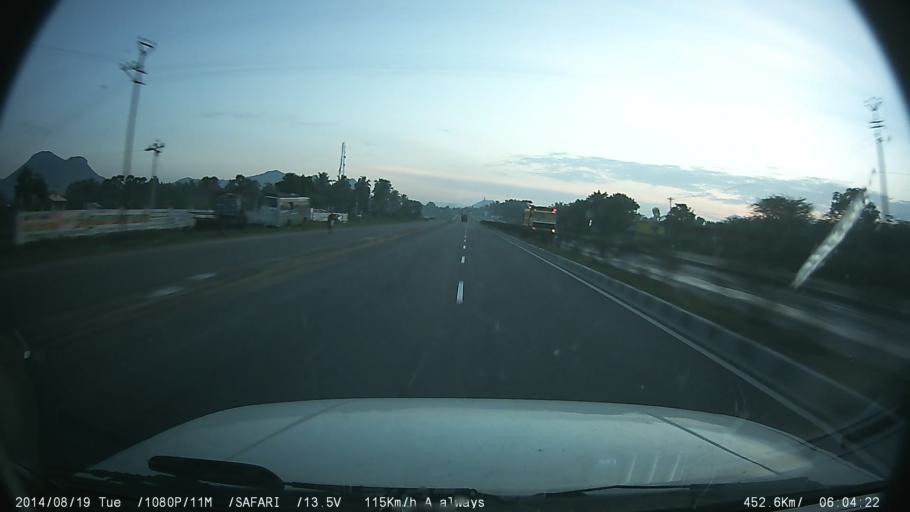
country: IN
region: Tamil Nadu
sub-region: Salem
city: Omalur
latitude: 11.8637
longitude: 78.0803
